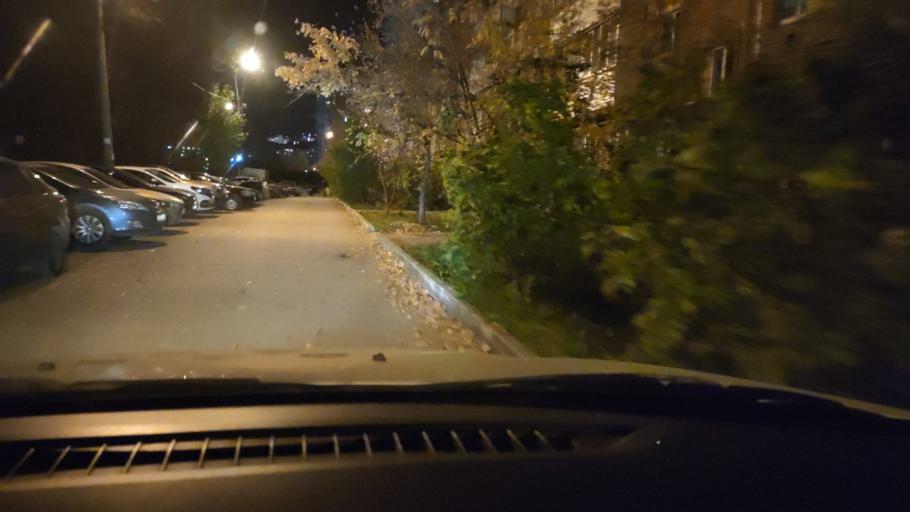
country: RU
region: Perm
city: Perm
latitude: 58.0163
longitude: 56.3033
